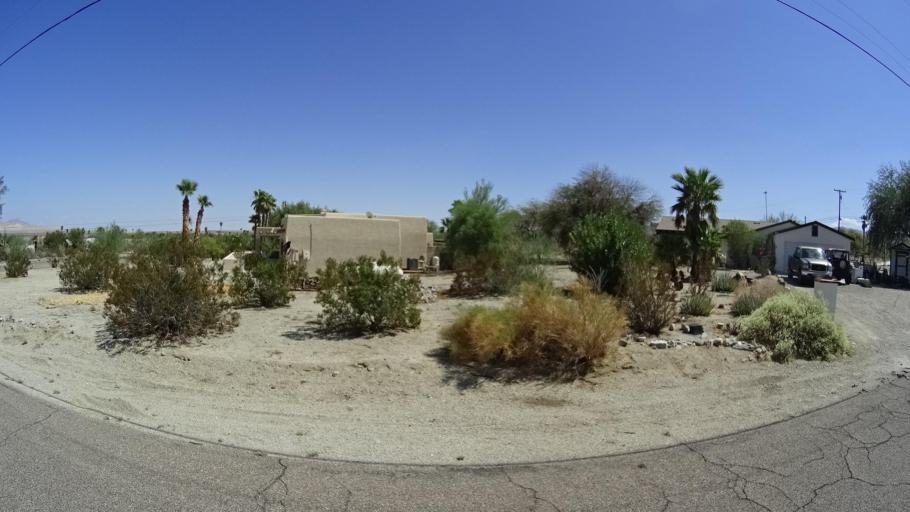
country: US
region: California
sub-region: San Diego County
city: Borrego Springs
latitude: 33.2080
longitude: -116.3397
